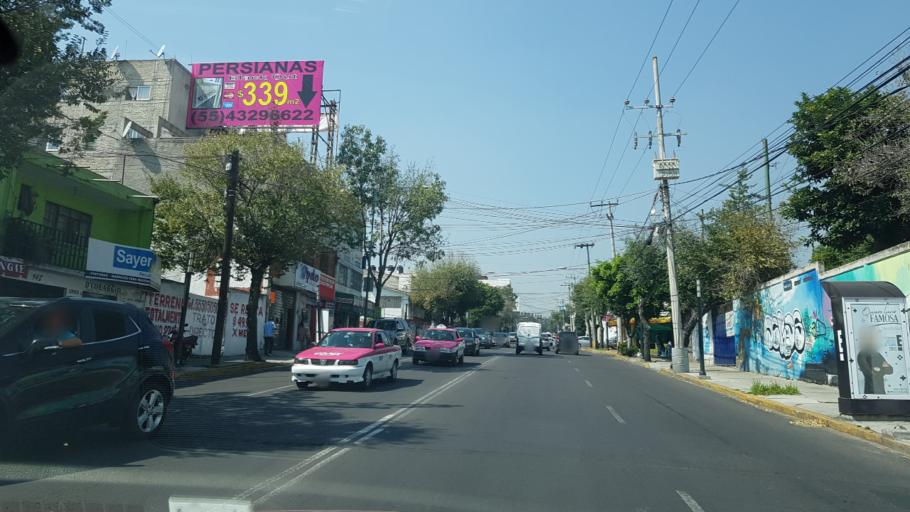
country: MX
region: Mexico City
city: Alvaro Obregon
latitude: 19.3510
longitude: -99.2190
